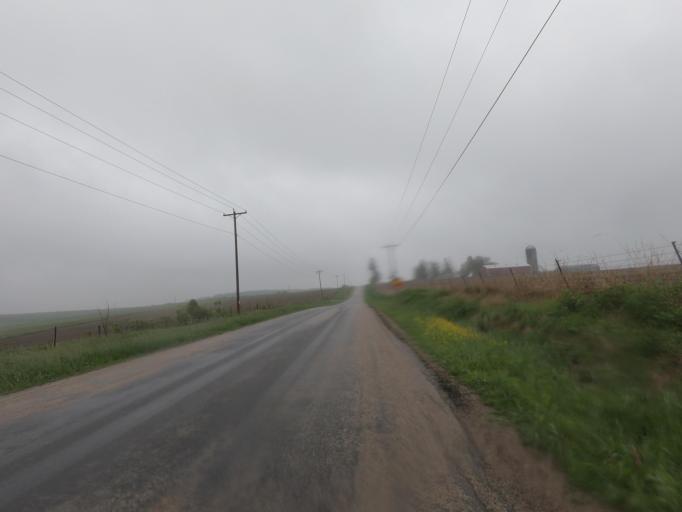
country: US
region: Wisconsin
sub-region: Grant County
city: Hazel Green
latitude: 42.5077
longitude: -90.5145
